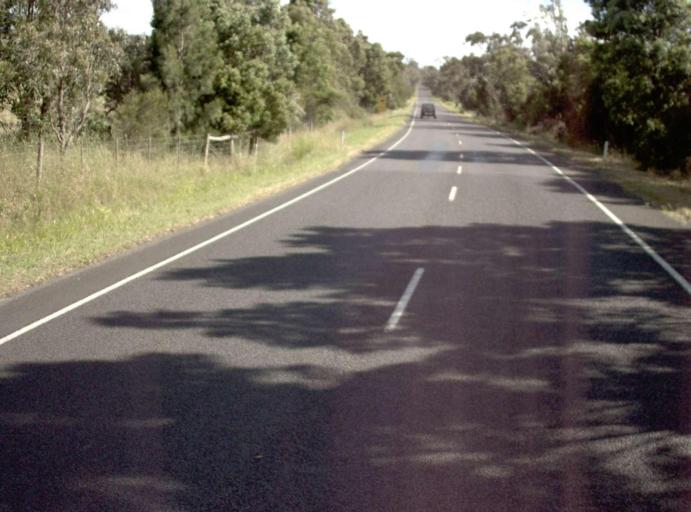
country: AU
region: Victoria
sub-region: Latrobe
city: Morwell
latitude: -38.1726
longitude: 146.4063
